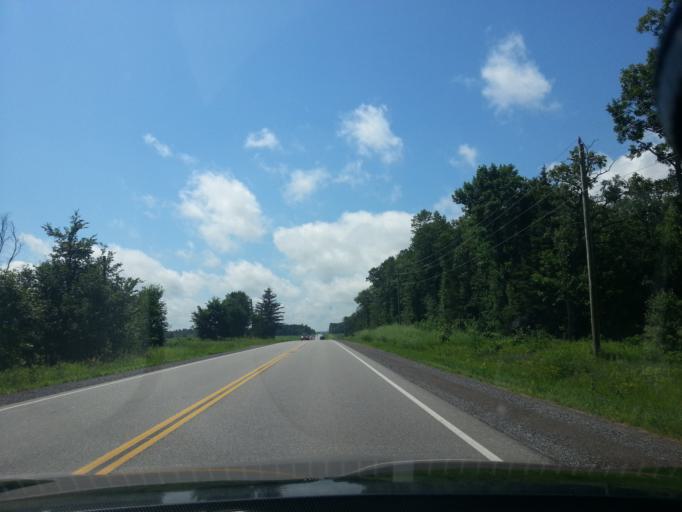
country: CA
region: Ontario
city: Renfrew
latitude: 45.5182
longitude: -76.8315
